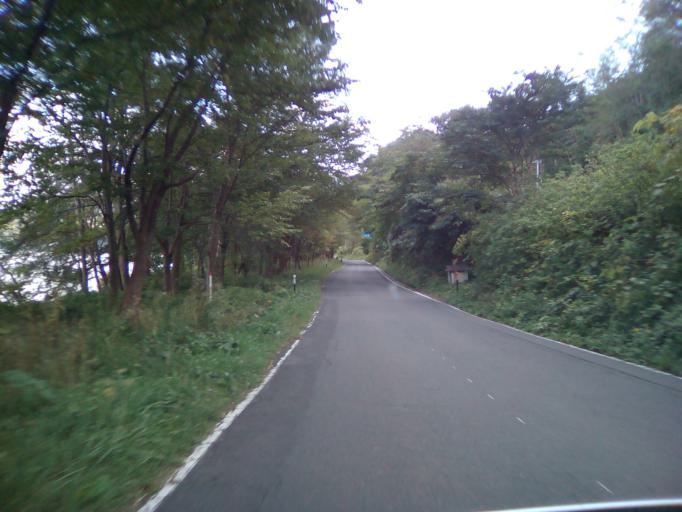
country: JP
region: Hokkaido
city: Date
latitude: 42.5812
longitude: 140.7959
